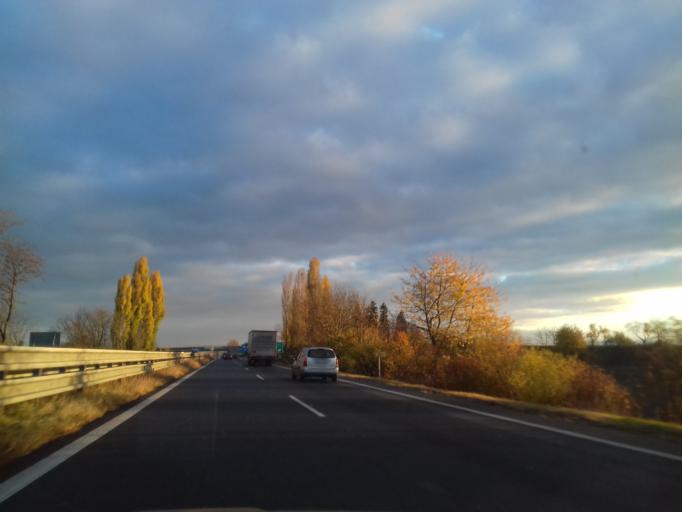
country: CZ
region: Olomoucky
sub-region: Okres Prostejov
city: Prostejov
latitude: 49.4406
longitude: 17.1108
